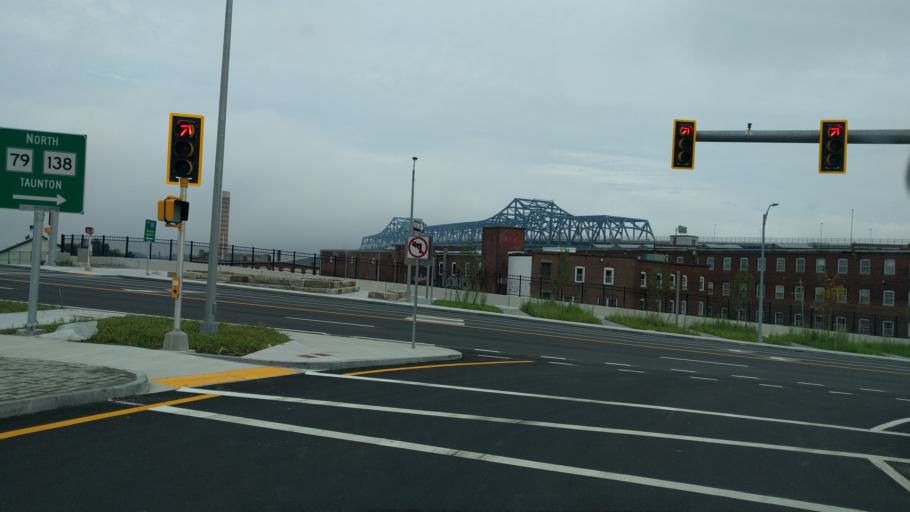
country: US
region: Massachusetts
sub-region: Bristol County
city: Fall River
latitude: 41.7013
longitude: -71.1617
